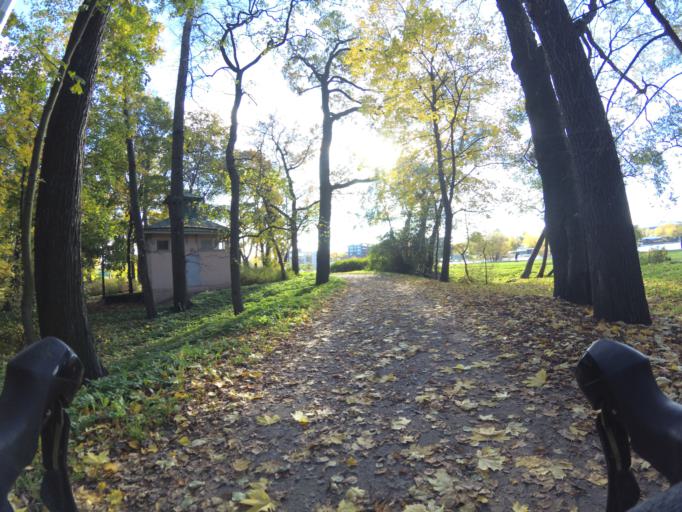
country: RU
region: St.-Petersburg
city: Staraya Derevnya
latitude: 59.9800
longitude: 30.2434
